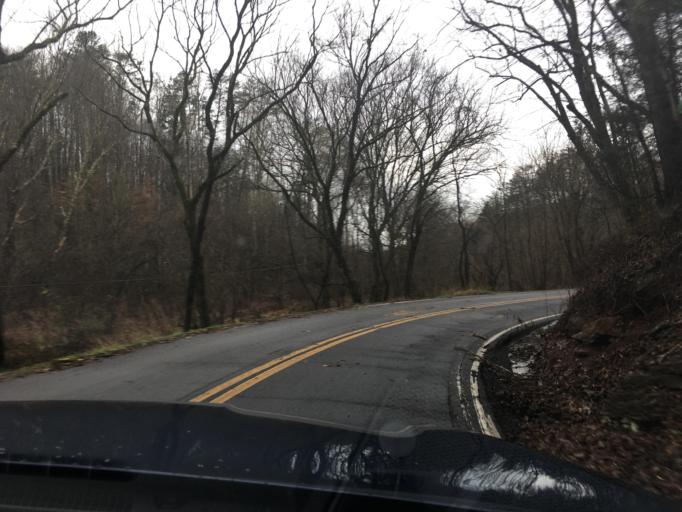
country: US
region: Tennessee
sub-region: McMinn County
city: Englewood
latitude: 35.3639
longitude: -84.4341
